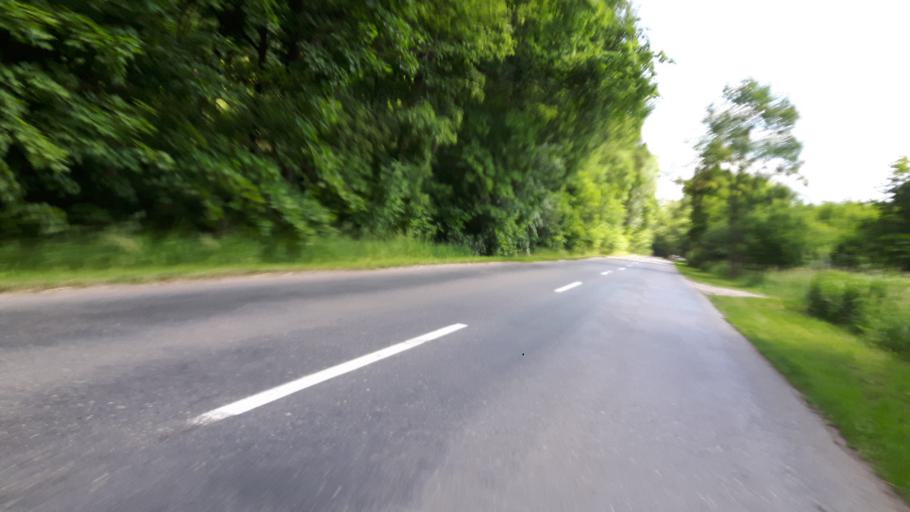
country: PL
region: Pomeranian Voivodeship
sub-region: Powiat gdanski
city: Cedry Wielkie
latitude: 54.3425
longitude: 18.8557
